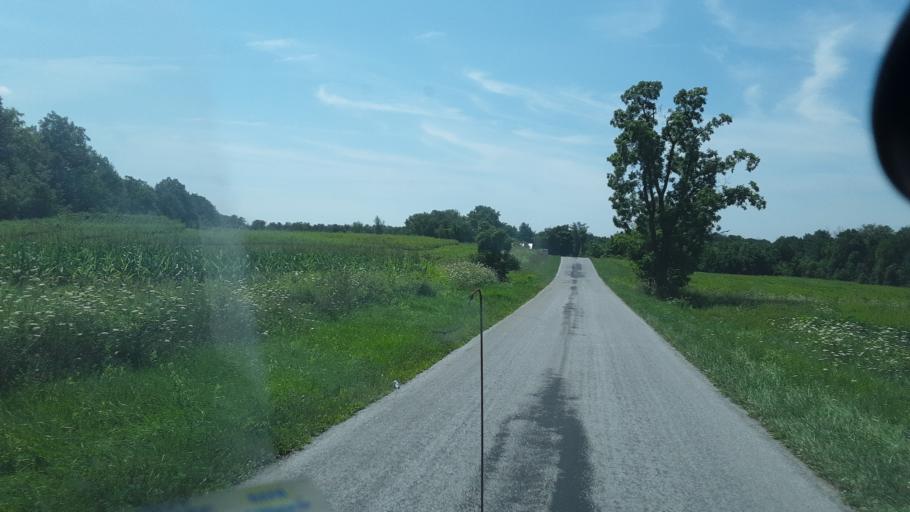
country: US
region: Ohio
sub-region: Hardin County
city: Forest
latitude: 40.7717
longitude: -83.5673
